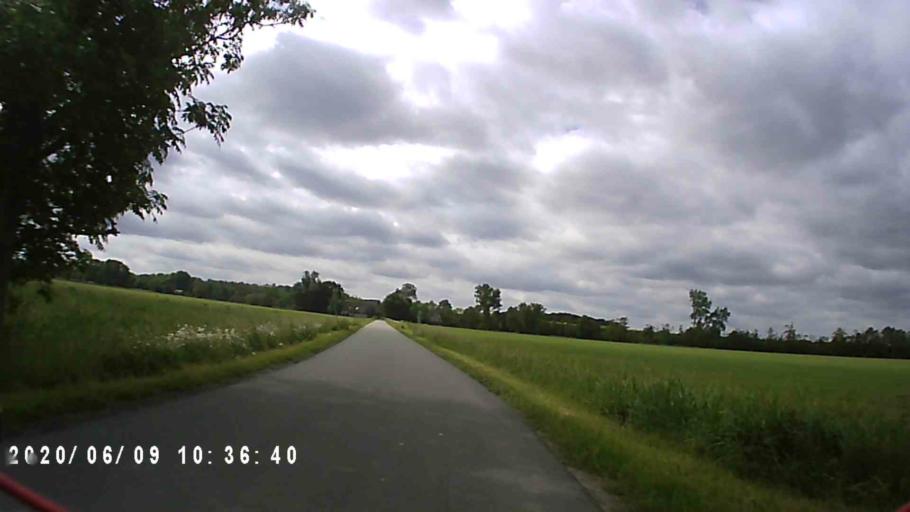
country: NL
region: Groningen
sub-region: Gemeente Groningen
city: Korrewegwijk
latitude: 53.2559
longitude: 6.5253
